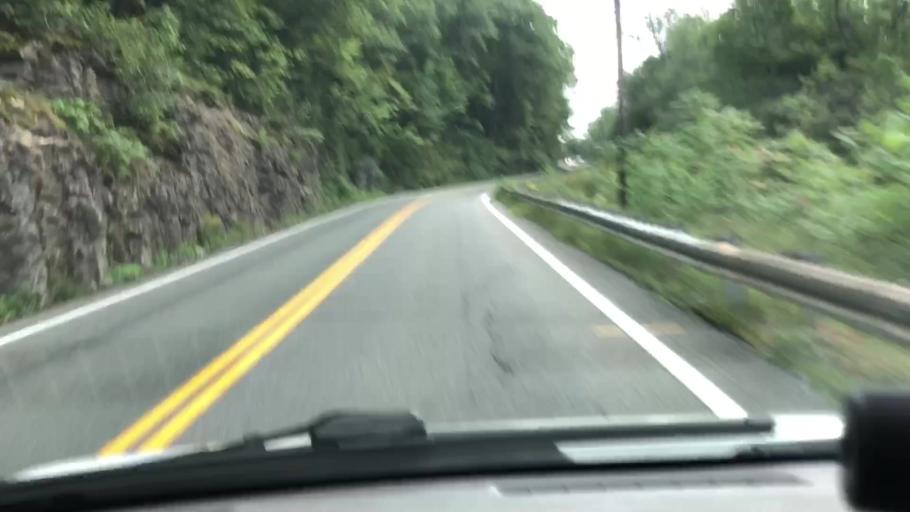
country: US
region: Massachusetts
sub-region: Berkshire County
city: North Adams
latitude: 42.7061
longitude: -73.0639
